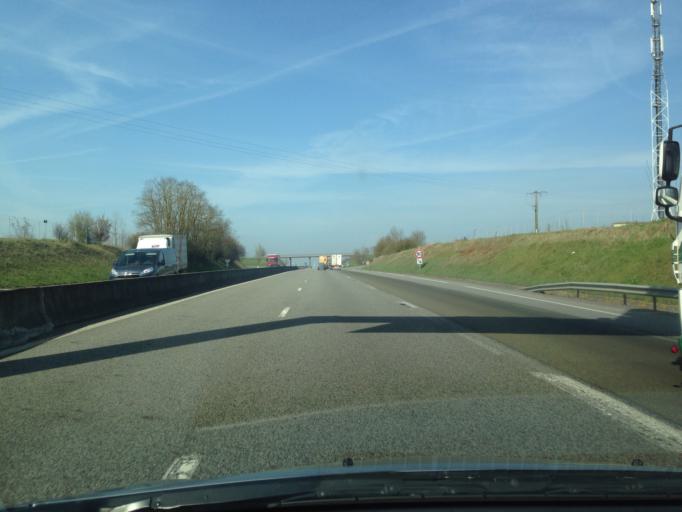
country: FR
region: Haute-Normandie
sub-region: Departement de la Seine-Maritime
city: Neufchatel-en-Bray
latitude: 49.7398
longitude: 1.4715
